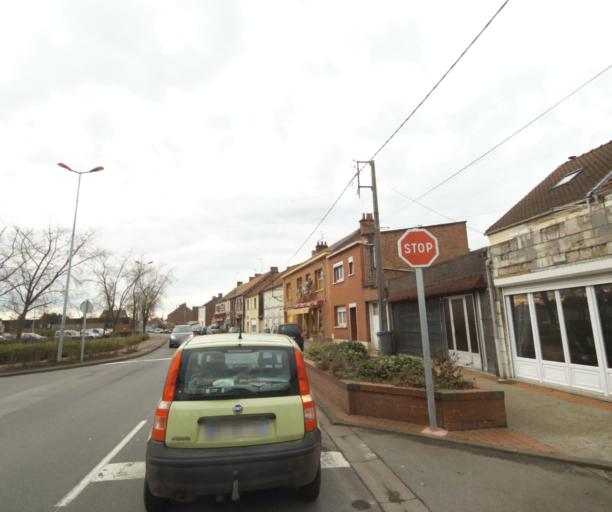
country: FR
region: Nord-Pas-de-Calais
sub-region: Departement du Nord
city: Vieux-Conde
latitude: 50.4776
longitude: 3.5752
